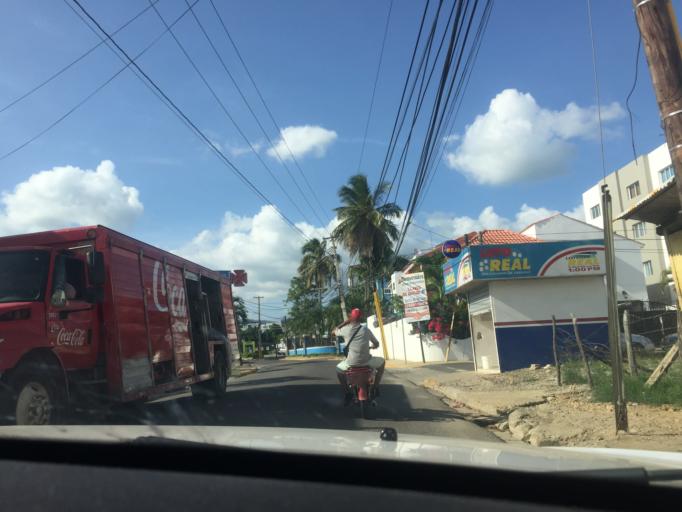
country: DO
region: Santiago
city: Tamboril
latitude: 19.4753
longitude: -70.6562
